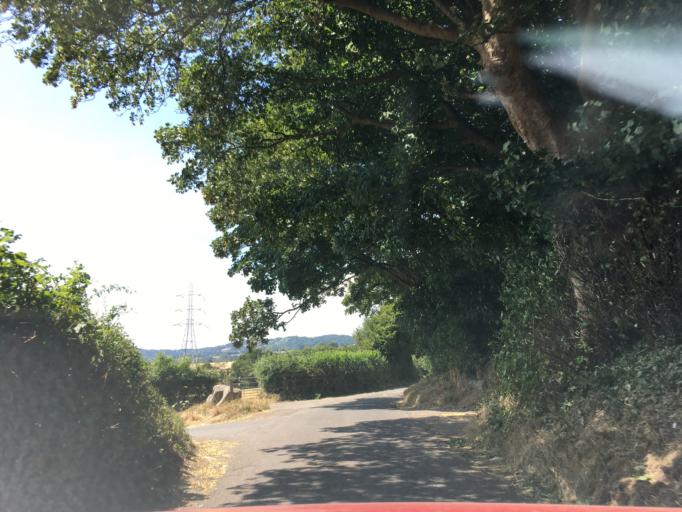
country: GB
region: Wales
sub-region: Caerphilly County Borough
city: Machen
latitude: 51.5473
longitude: -3.1386
